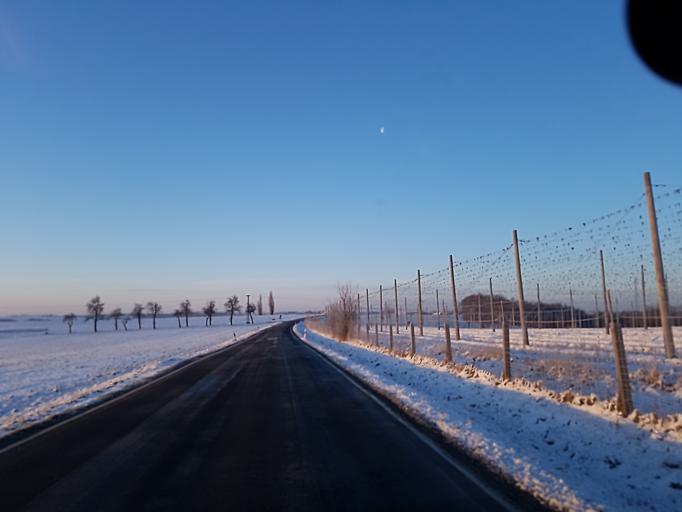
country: DE
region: Saxony
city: Grossweitzschen
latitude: 51.1998
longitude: 13.0753
